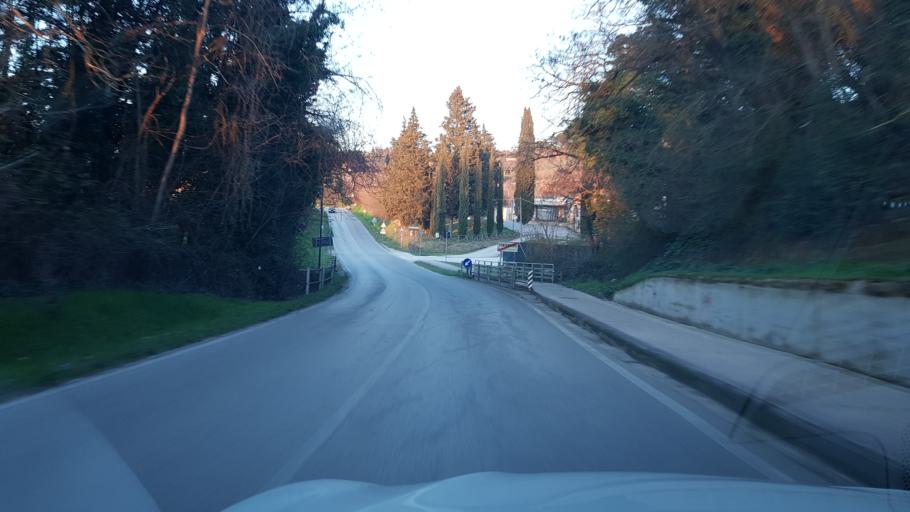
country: IT
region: Umbria
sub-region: Provincia di Perugia
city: Torgiano
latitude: 43.0117
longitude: 12.4344
